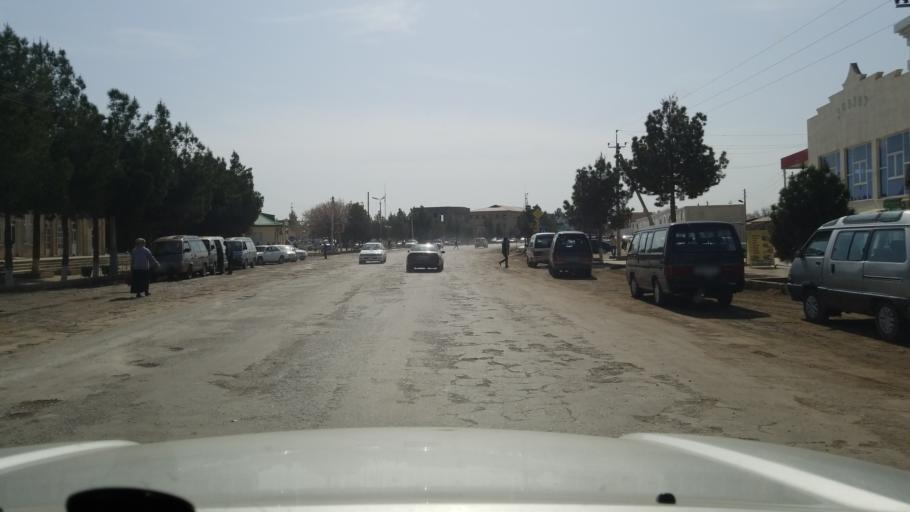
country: TM
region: Lebap
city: Sayat
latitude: 38.7799
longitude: 63.8805
